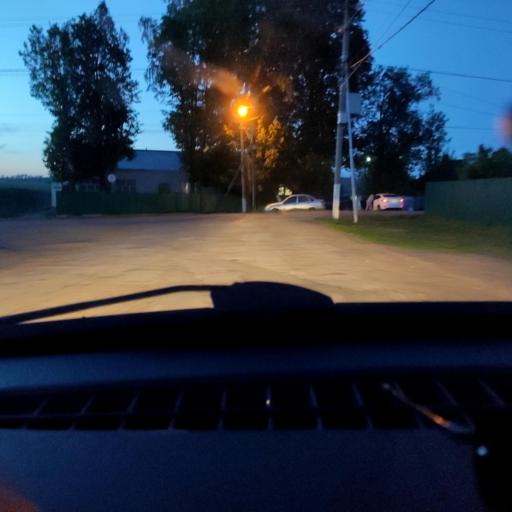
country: RU
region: Bashkortostan
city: Karmaskaly
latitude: 54.3706
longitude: 56.1653
